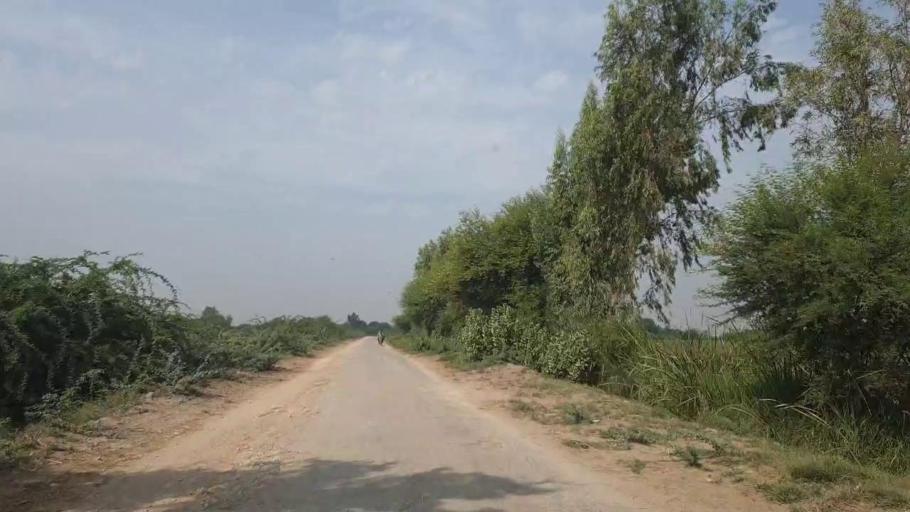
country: PK
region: Sindh
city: Tando Bago
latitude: 24.9245
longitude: 68.9907
